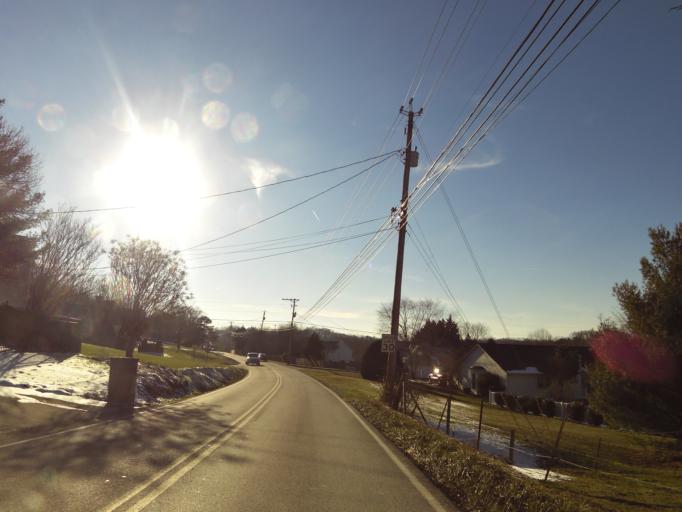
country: US
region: Tennessee
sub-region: Knox County
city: Farragut
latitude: 35.9554
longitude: -84.0582
